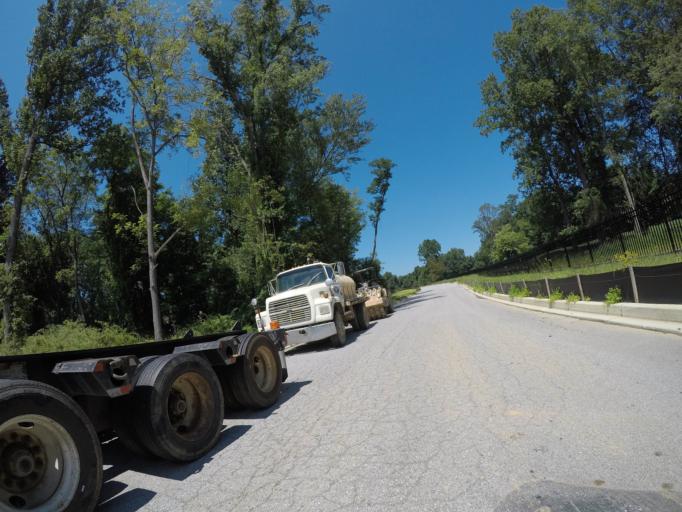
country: US
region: Maryland
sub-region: Howard County
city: Columbia
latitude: 39.2983
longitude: -76.8699
